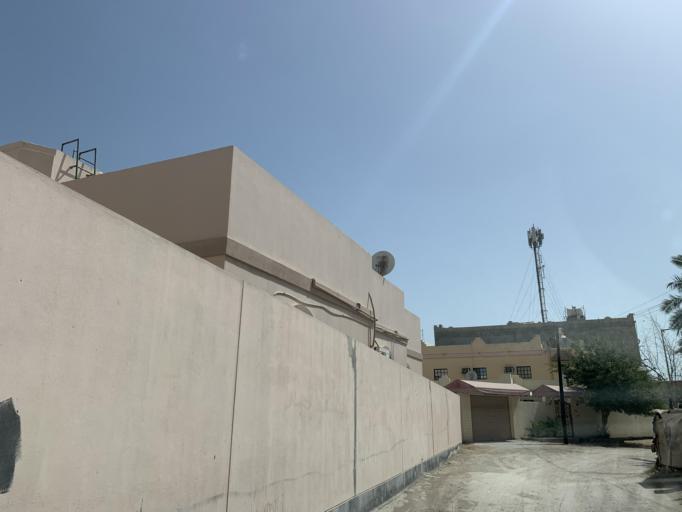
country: BH
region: Northern
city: Sitrah
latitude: 26.1428
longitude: 50.6058
